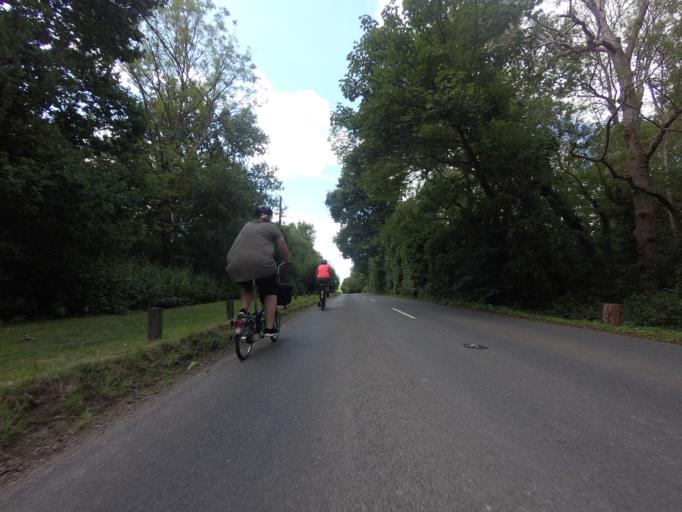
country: GB
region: England
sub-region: East Sussex
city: Hailsham
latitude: 50.8487
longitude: 0.1703
